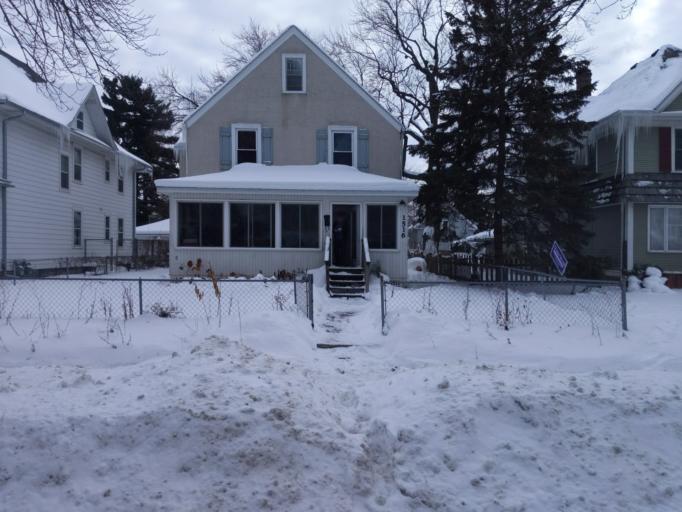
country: US
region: Minnesota
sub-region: Ramsey County
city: Falcon Heights
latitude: 44.9628
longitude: -93.1647
